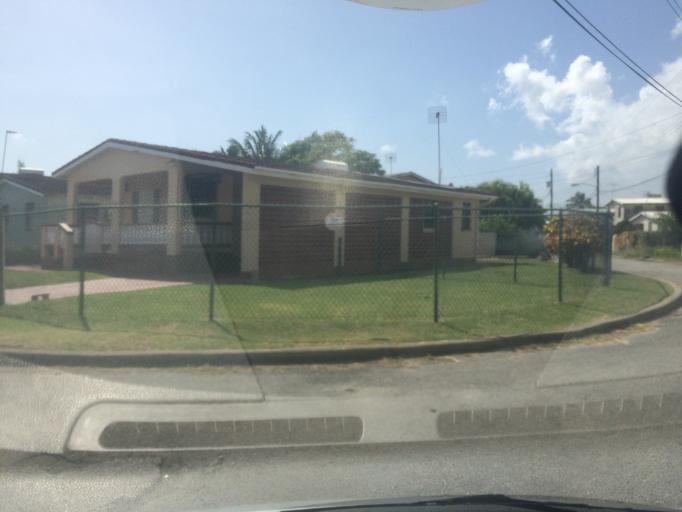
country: BB
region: Christ Church
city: Oistins
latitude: 13.0647
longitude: -59.5040
